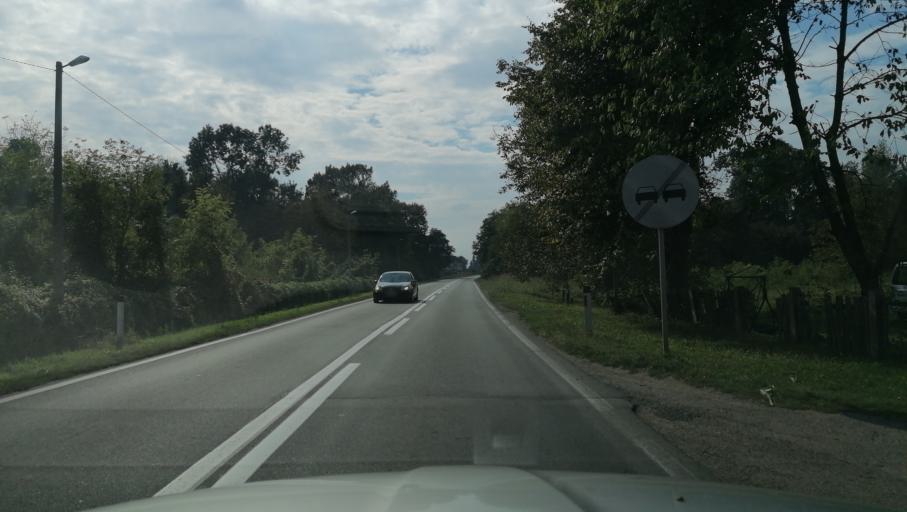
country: BA
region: Republika Srpska
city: Dvorovi
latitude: 44.8313
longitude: 19.2929
